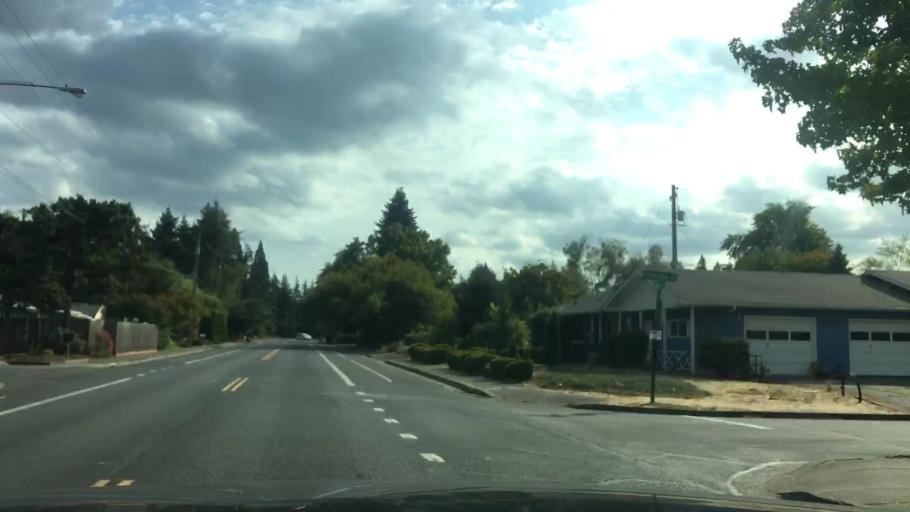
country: US
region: Oregon
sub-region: Lane County
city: Eugene
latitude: 44.0863
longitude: -123.0881
